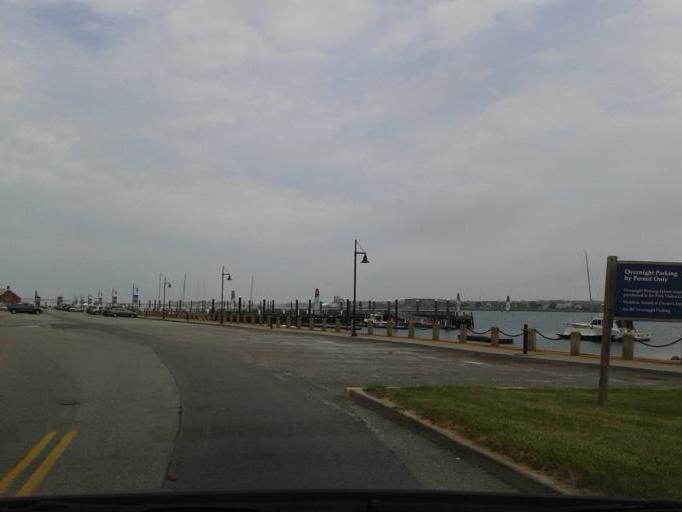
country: US
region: Rhode Island
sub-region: Newport County
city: Newport
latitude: 41.4761
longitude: -71.3353
